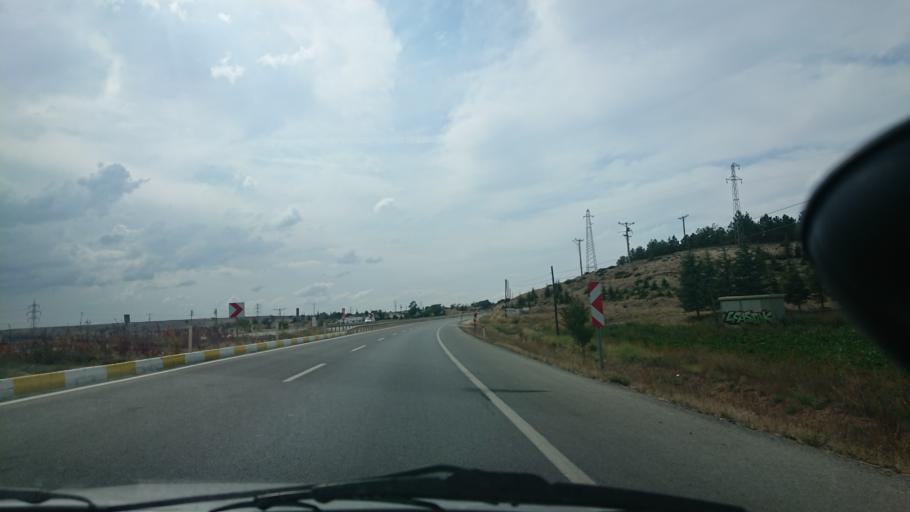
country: TR
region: Eskisehir
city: Eskisehir
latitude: 39.7252
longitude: 30.3450
